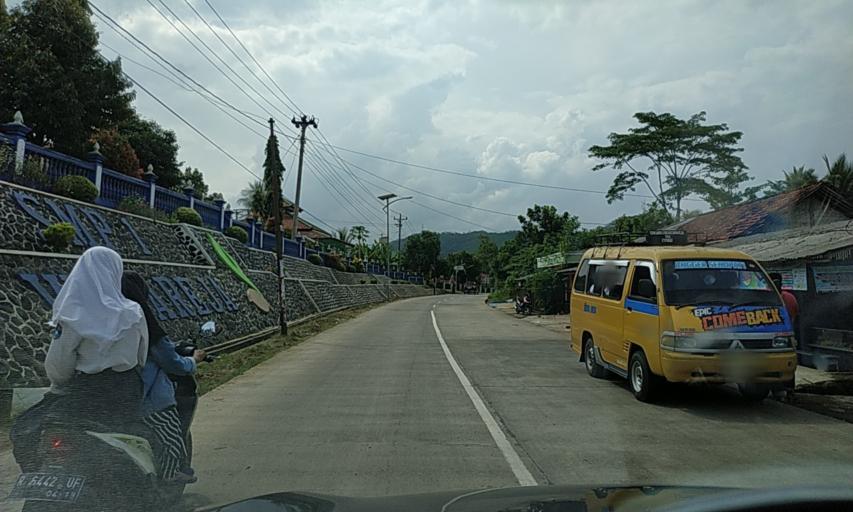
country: ID
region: Central Java
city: Winangun
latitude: -7.3489
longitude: 108.7083
